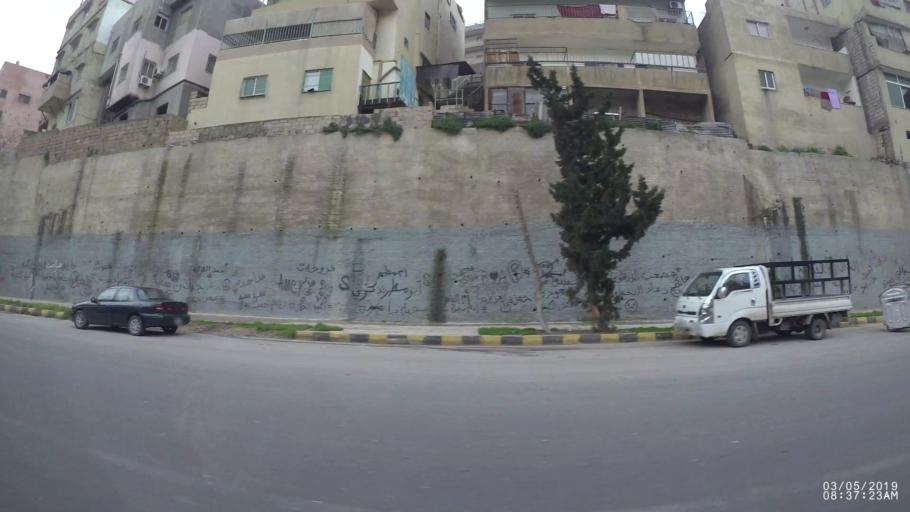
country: JO
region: Amman
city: Amman
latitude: 31.9561
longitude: 35.9391
